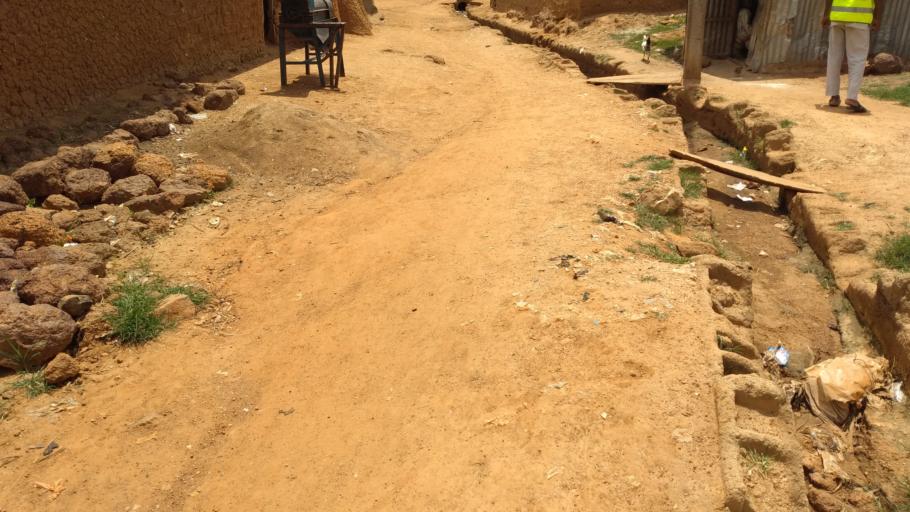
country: NG
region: Katsina
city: Sabuwa
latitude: 11.0336
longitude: 7.0867
